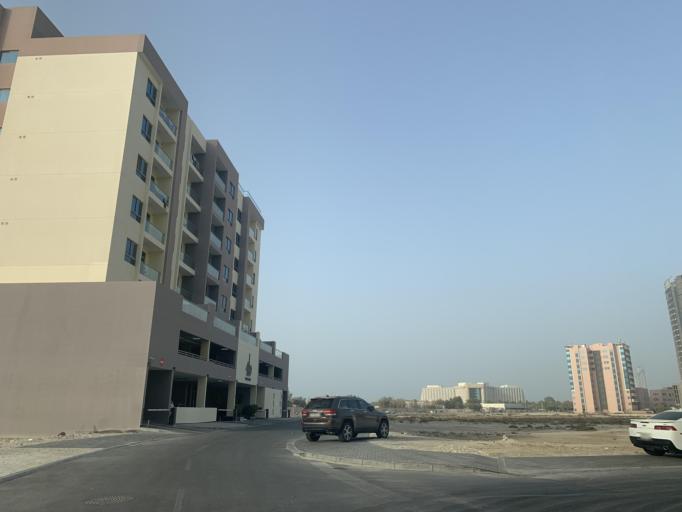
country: BH
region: Manama
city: Jidd Hafs
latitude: 26.2414
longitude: 50.5321
